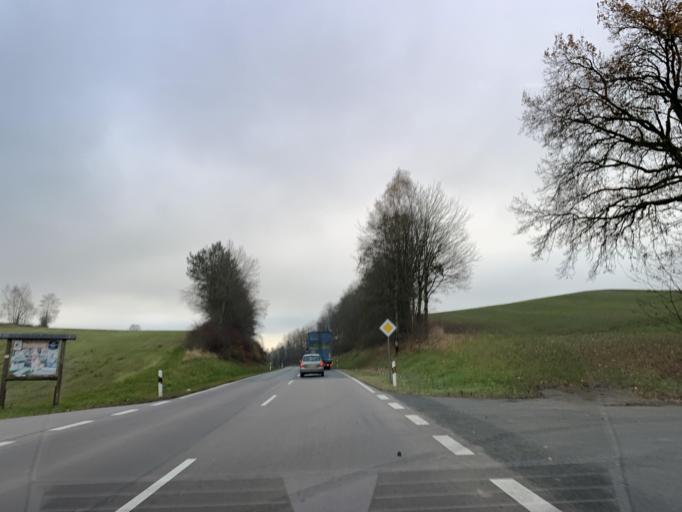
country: DE
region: Bavaria
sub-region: Upper Palatinate
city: Roetz
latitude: 49.3457
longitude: 12.5010
